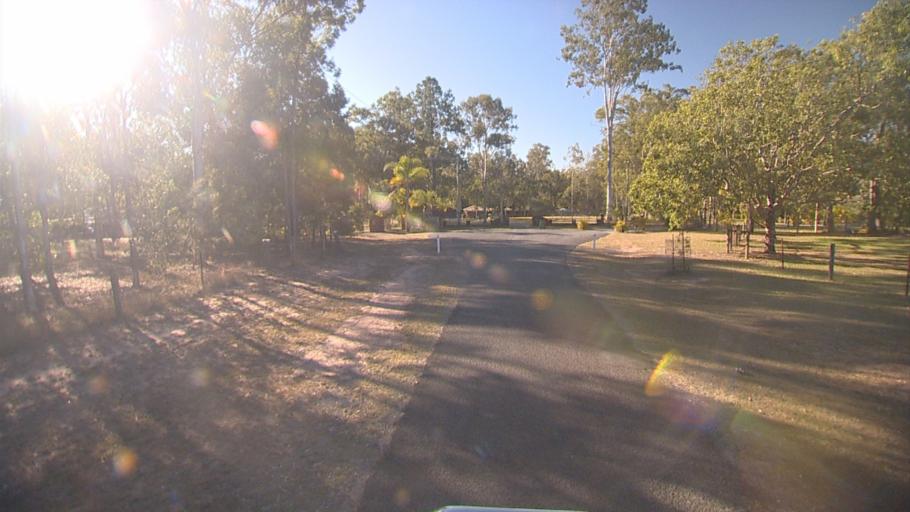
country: AU
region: Queensland
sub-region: Logan
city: North Maclean
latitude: -27.7541
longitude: 153.0098
